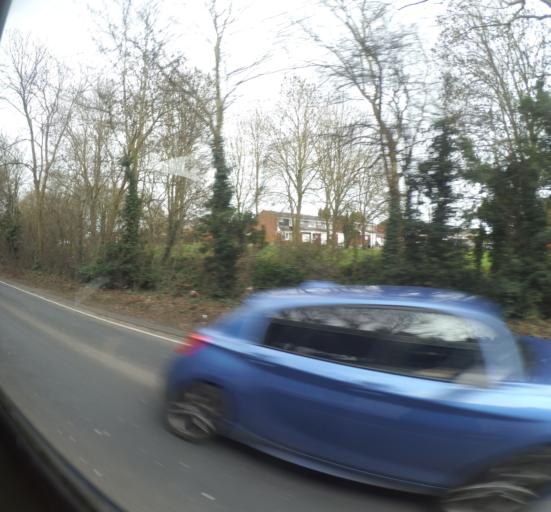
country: GB
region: England
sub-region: Warwickshire
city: Ryton on Dunsmore
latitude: 52.4146
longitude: -1.4448
